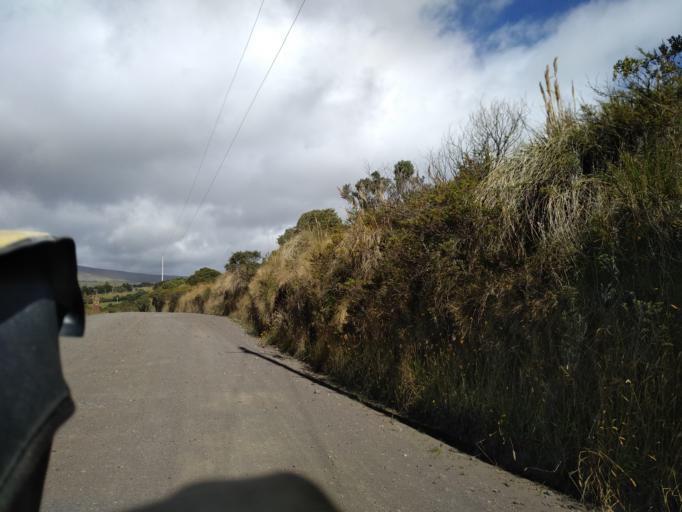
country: EC
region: Pichincha
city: Machachi
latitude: -0.5405
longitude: -78.4725
